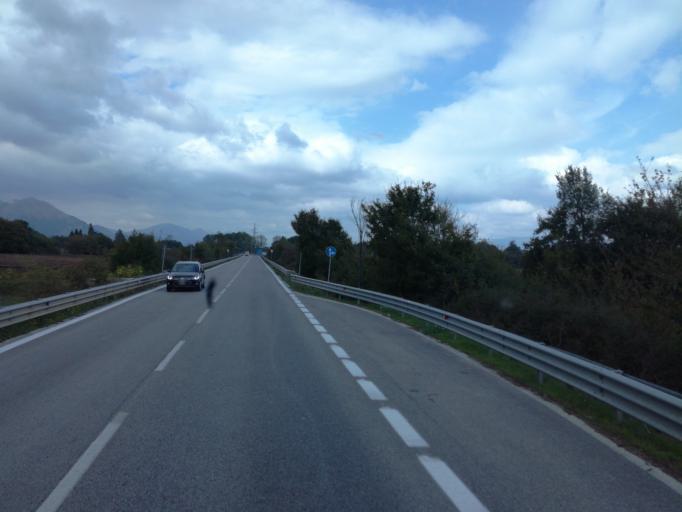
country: IT
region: Molise
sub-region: Provincia di Campobasso
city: Guardiaregia
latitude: 41.4697
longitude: 14.5427
